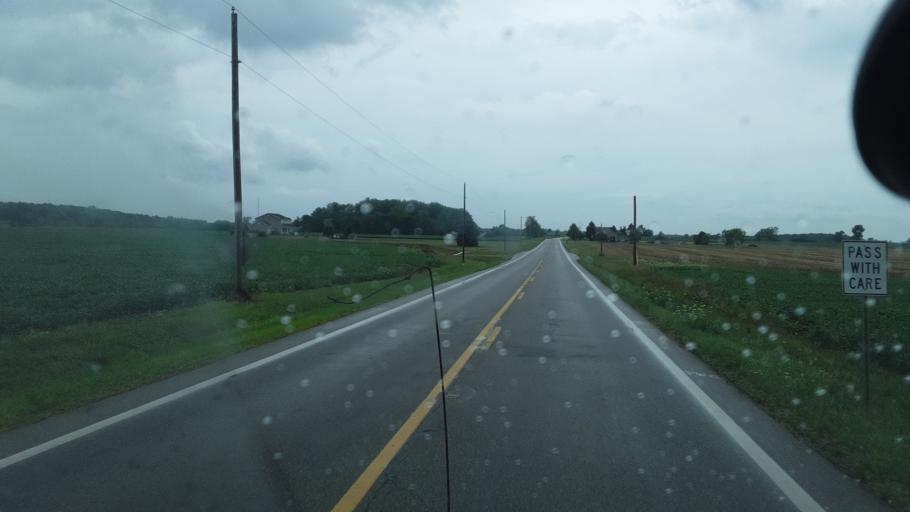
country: US
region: Indiana
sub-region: Steuben County
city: Hamilton
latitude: 41.5564
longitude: -84.7972
